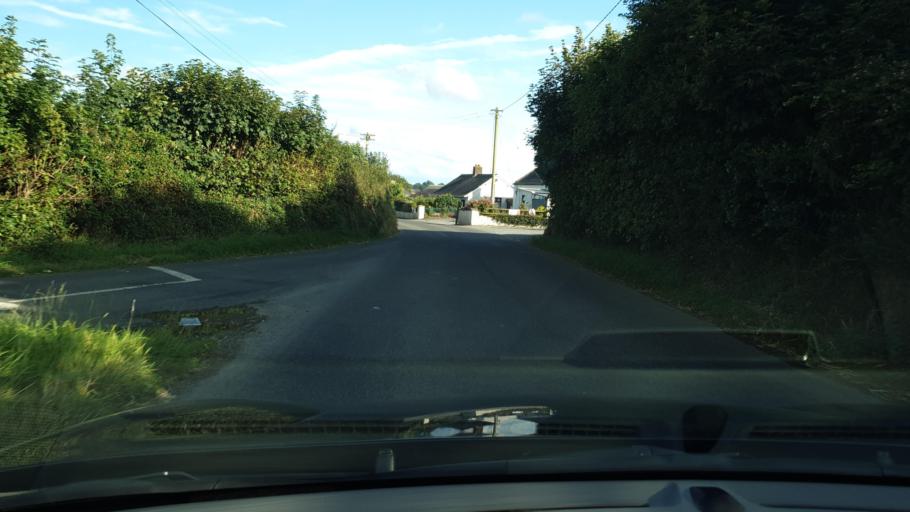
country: IE
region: Leinster
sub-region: An Mhi
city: Stamullin
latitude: 53.6169
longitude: -6.3205
